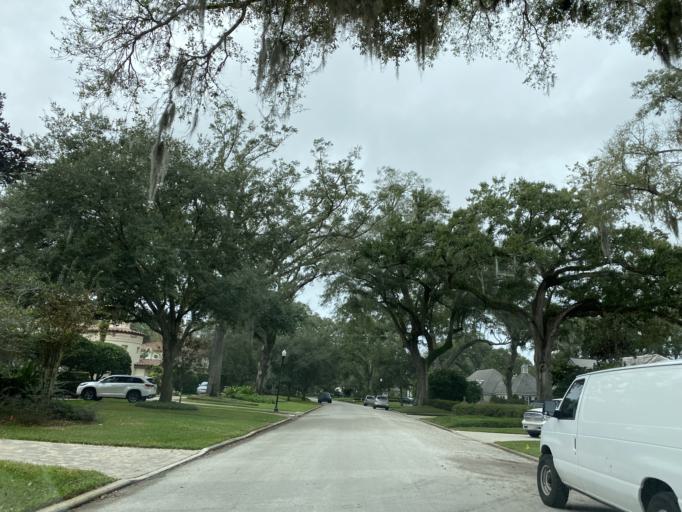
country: US
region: Florida
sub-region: Orange County
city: Orlando
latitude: 28.5559
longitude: -81.3895
